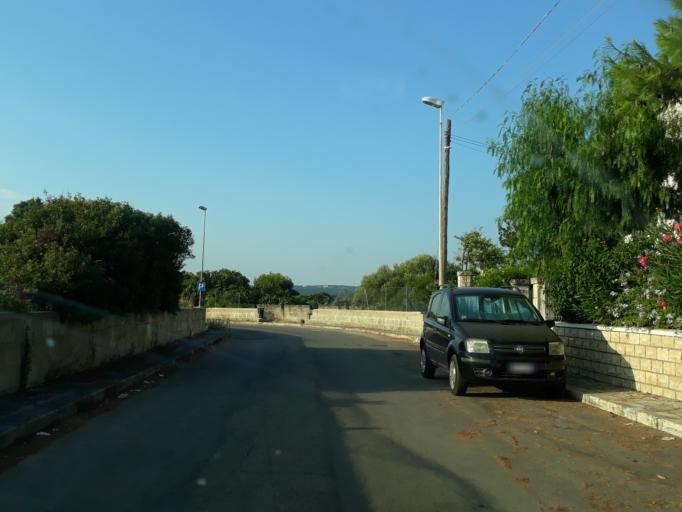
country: IT
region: Apulia
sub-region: Provincia di Brindisi
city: Carovigno
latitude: 40.7552
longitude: 17.7044
